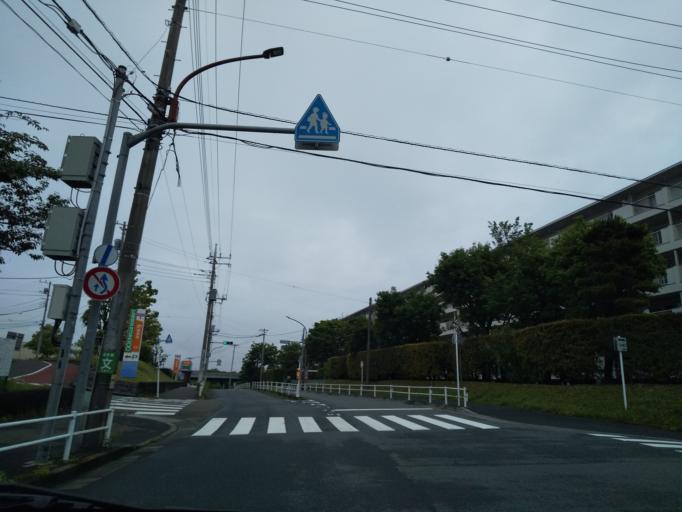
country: JP
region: Tokyo
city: Hino
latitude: 35.6538
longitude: 139.4161
